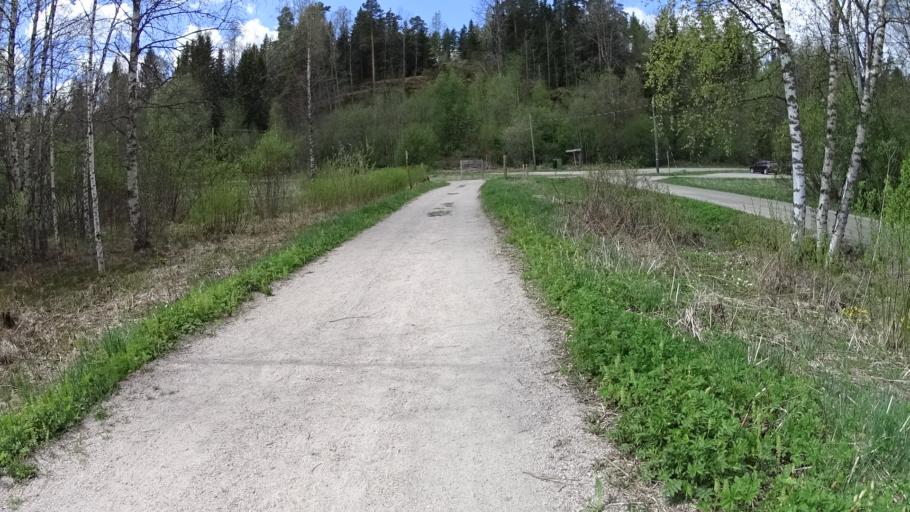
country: FI
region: Uusimaa
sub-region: Helsinki
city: Vihti
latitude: 60.3740
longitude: 24.4983
